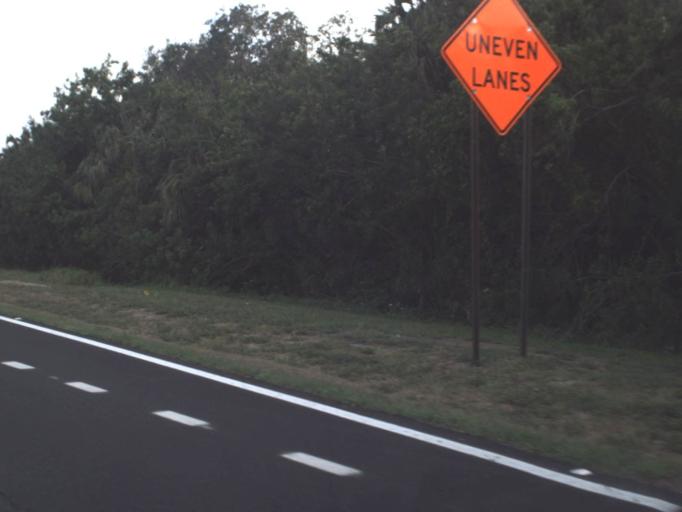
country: US
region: Florida
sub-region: Brevard County
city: Port Saint John
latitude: 28.5312
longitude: -80.7907
